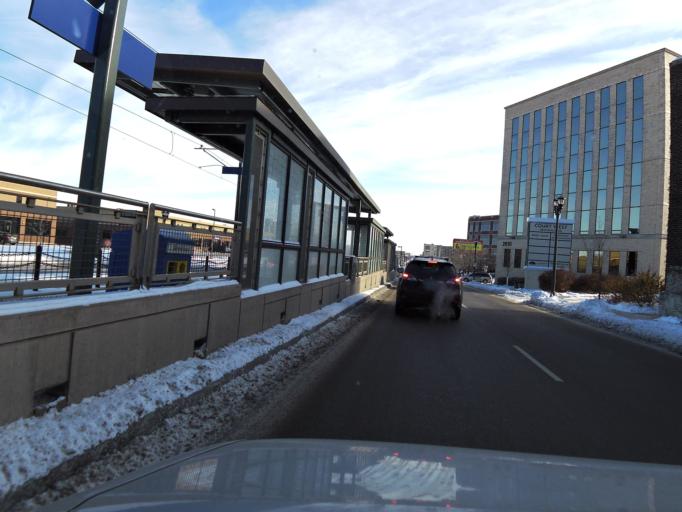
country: US
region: Minnesota
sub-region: Ramsey County
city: Lauderdale
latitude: 44.9671
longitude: -93.2059
